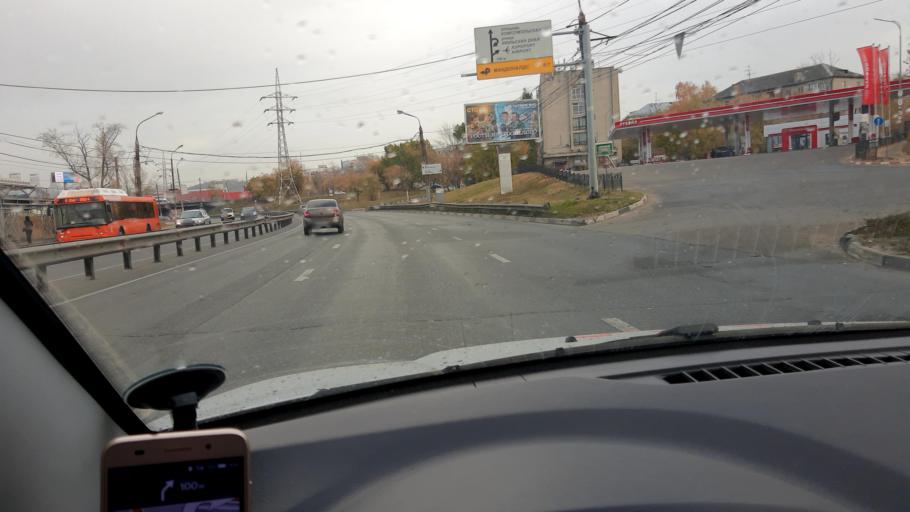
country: RU
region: Nizjnij Novgorod
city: Nizhniy Novgorod
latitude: 56.2958
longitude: 43.9301
